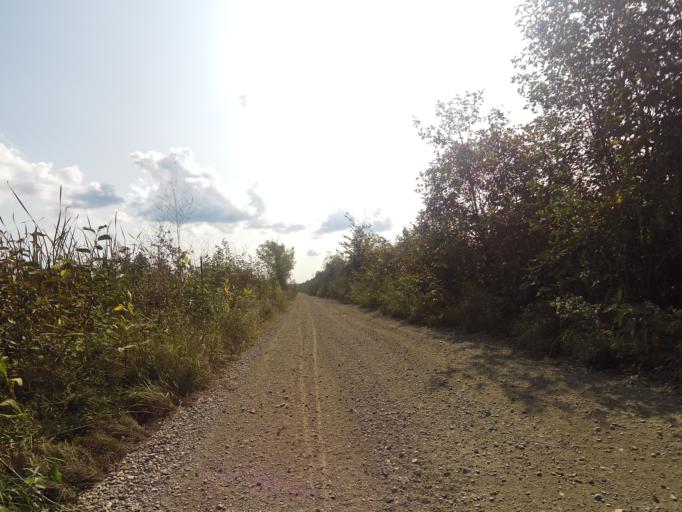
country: CA
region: Ontario
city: Renfrew
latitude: 45.1329
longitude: -76.6870
